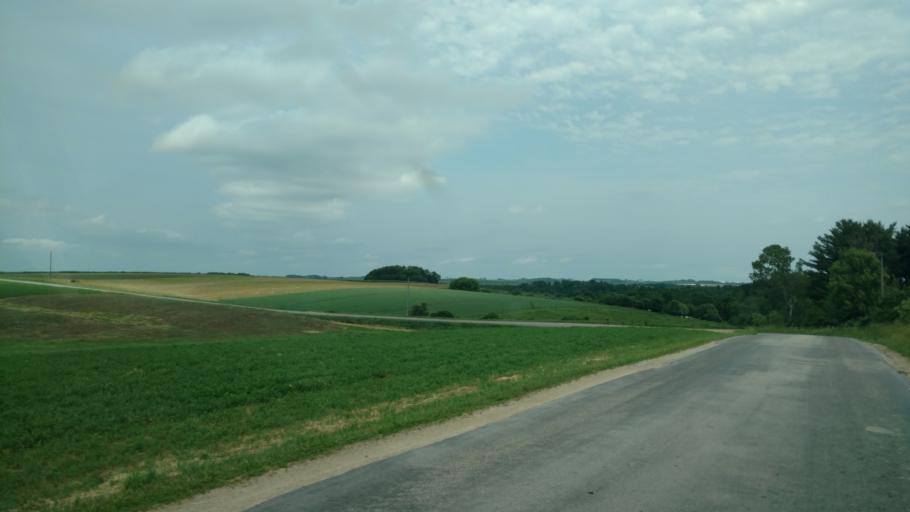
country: US
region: Wisconsin
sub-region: Monroe County
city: Cashton
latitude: 43.7135
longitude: -90.7104
